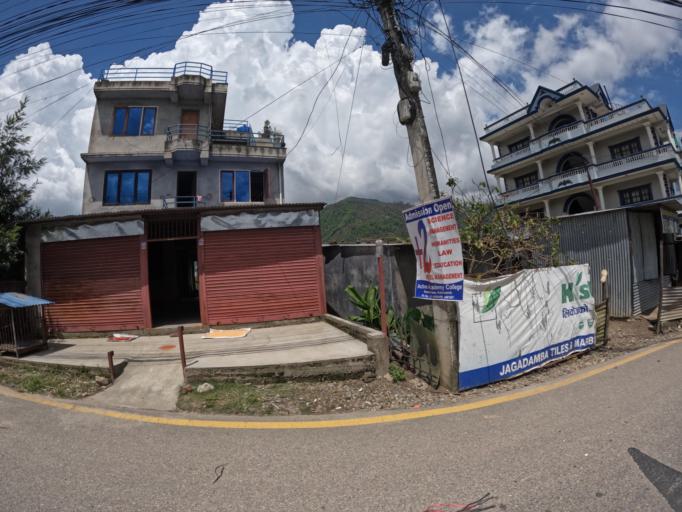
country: NP
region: Central Region
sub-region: Bagmati Zone
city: Kathmandu
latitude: 27.7772
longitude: 85.3267
